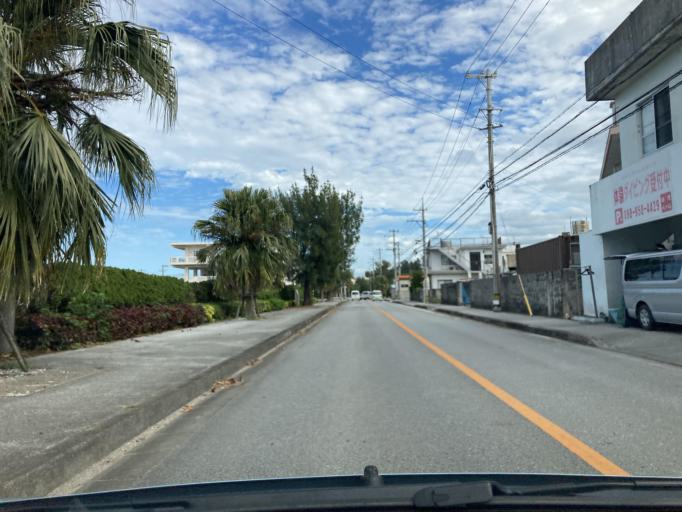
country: JP
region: Okinawa
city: Ishikawa
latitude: 26.4360
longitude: 127.7627
